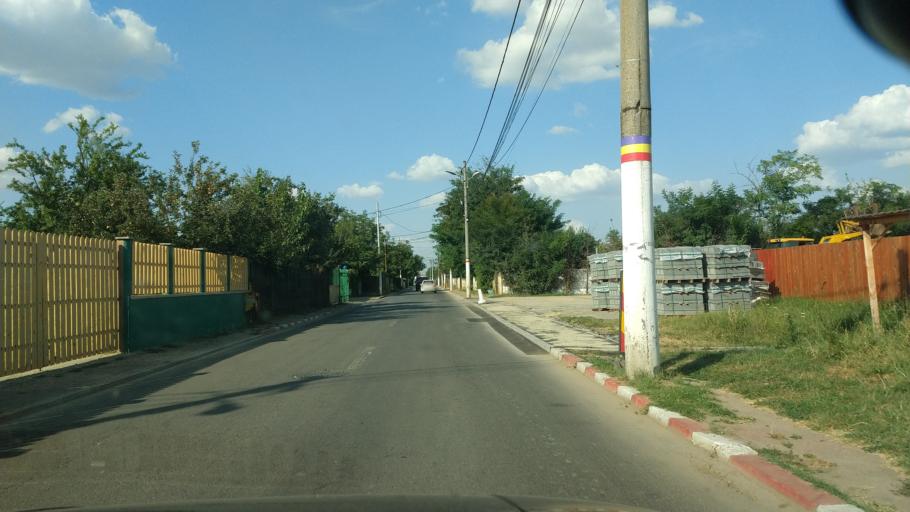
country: RO
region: Ilfov
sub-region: Voluntari City
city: Voluntari
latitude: 44.4925
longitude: 26.1589
